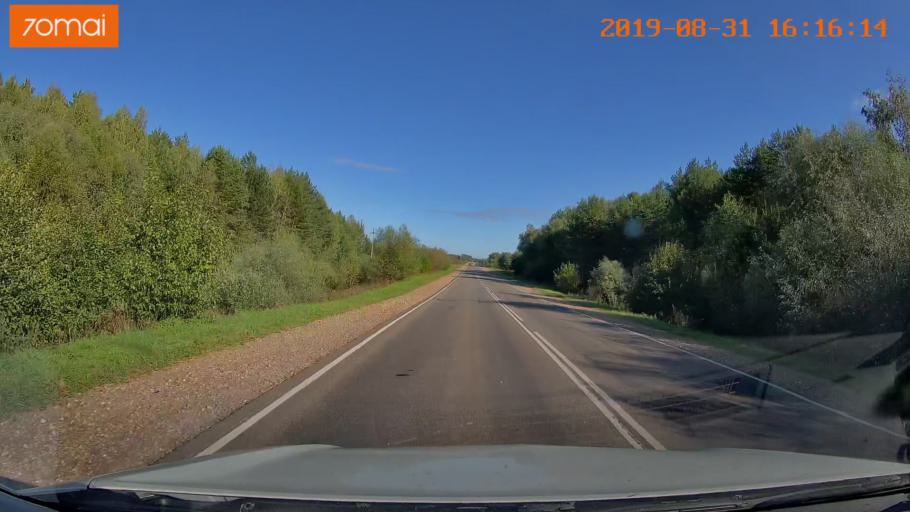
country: RU
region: Kaluga
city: Nikola-Lenivets
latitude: 54.5543
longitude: 35.5058
